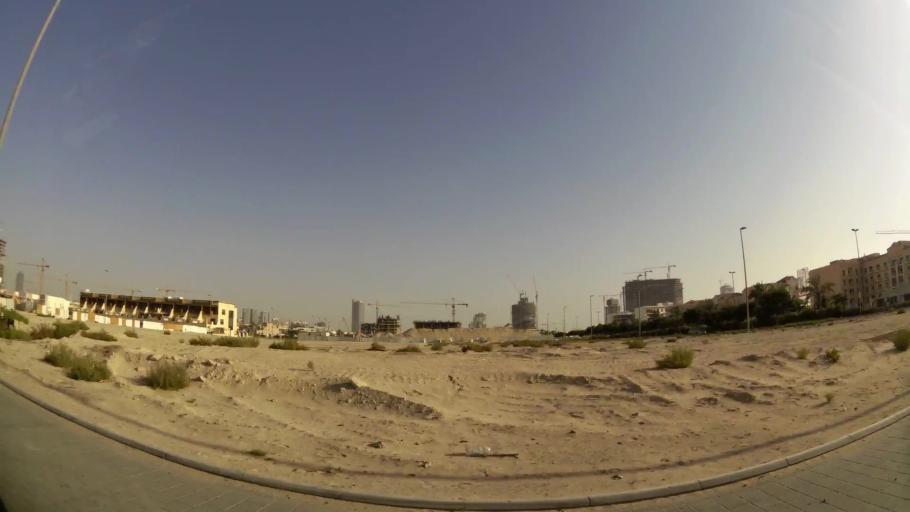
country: AE
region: Dubai
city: Dubai
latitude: 25.0641
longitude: 55.2097
